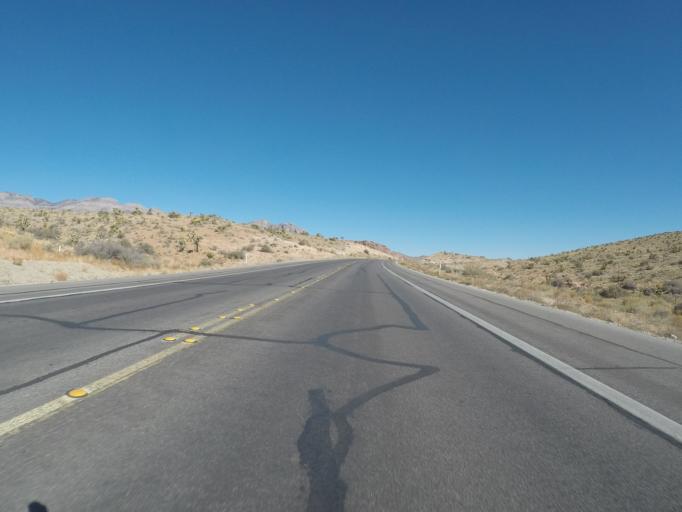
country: US
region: Nevada
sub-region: Clark County
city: Summerlin South
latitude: 36.1245
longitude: -115.4326
